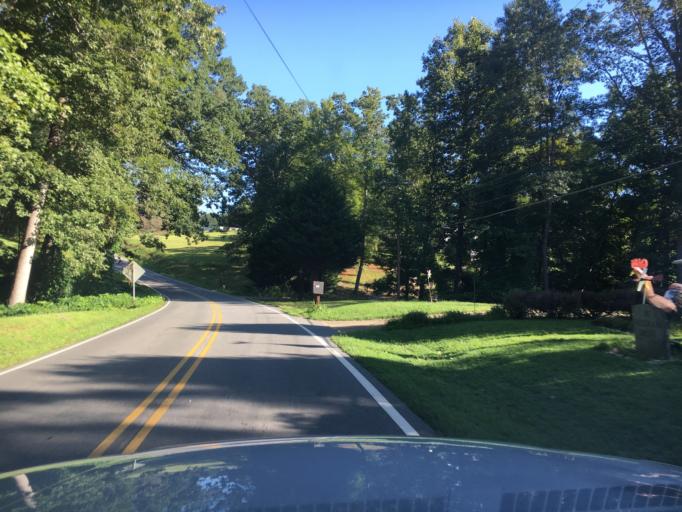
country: US
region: North Carolina
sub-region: McDowell County
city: West Marion
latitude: 35.6553
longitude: -82.0313
